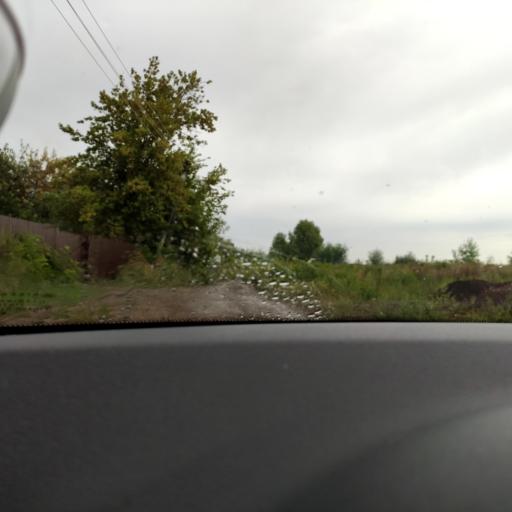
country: RU
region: Samara
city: Samara
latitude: 53.1708
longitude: 50.1622
